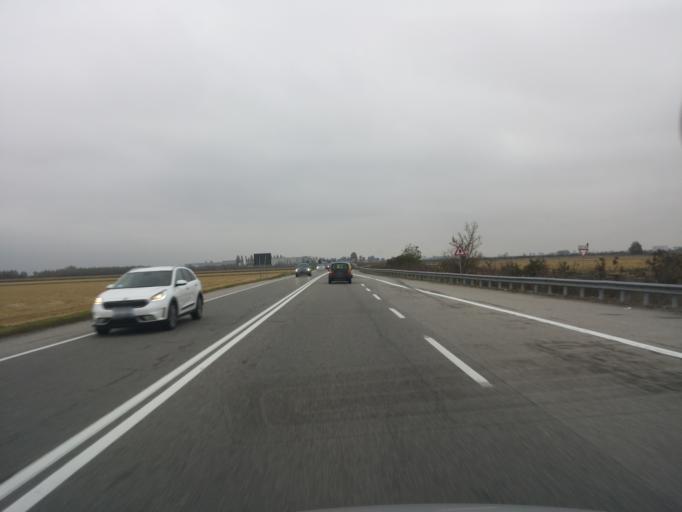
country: IT
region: Piedmont
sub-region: Provincia di Vercelli
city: Borgo Vercelli
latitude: 45.3731
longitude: 8.4891
